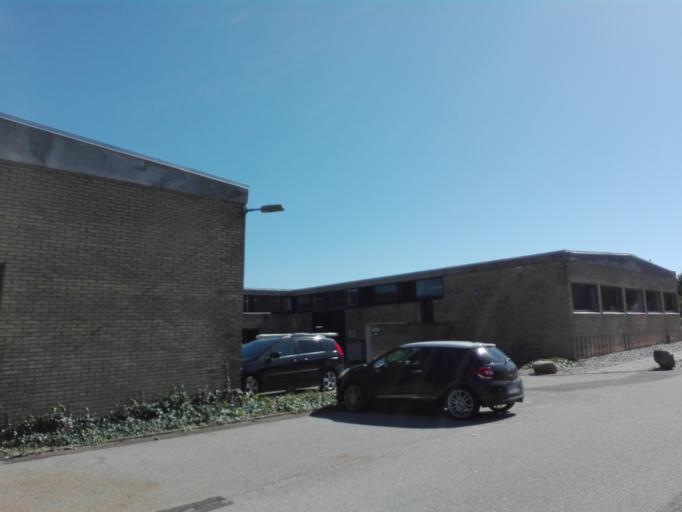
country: DK
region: Central Jutland
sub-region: Arhus Kommune
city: Tranbjerg
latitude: 56.1094
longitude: 10.1545
